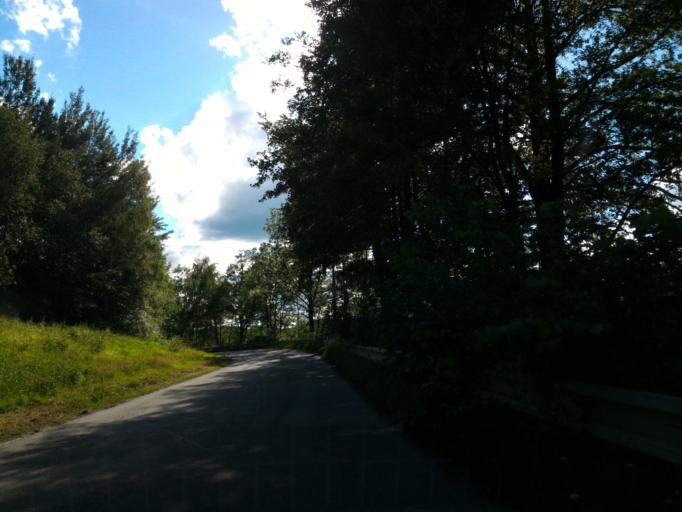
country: CZ
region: Vysocina
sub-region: Okres Jihlava
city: Telc
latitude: 49.2357
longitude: 15.4333
